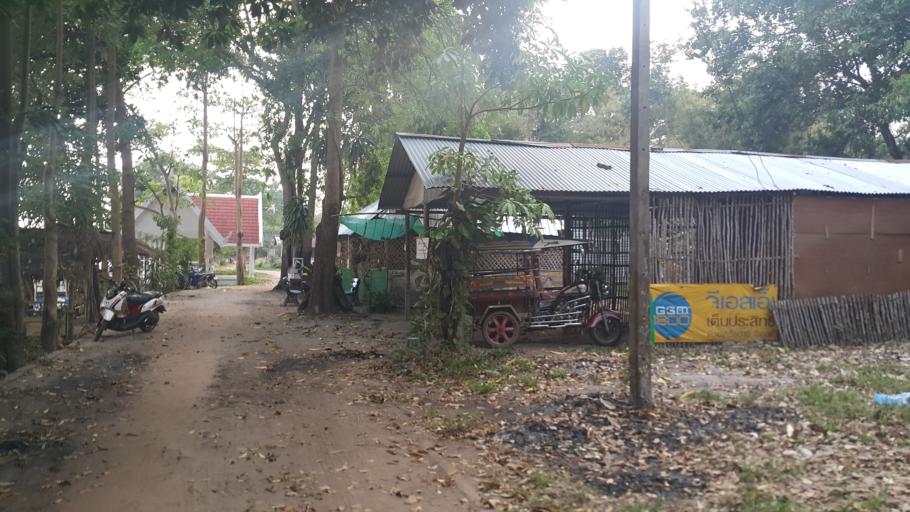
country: TH
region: Nong Khai
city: Bueng Khong Long
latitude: 17.9795
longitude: 104.0275
